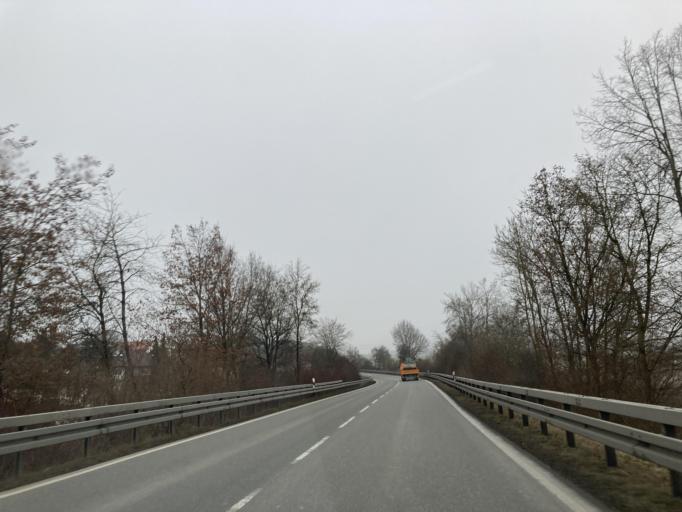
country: DE
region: Baden-Wuerttemberg
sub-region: Freiburg Region
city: Buchheim
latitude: 47.9877
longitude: 9.0006
